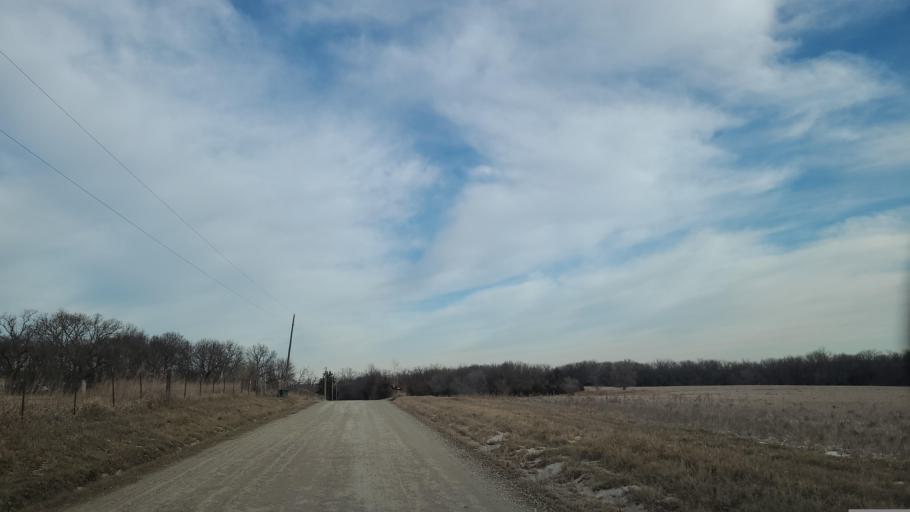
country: US
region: Kansas
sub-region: Jefferson County
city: Oskaloosa
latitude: 39.0521
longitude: -95.4098
